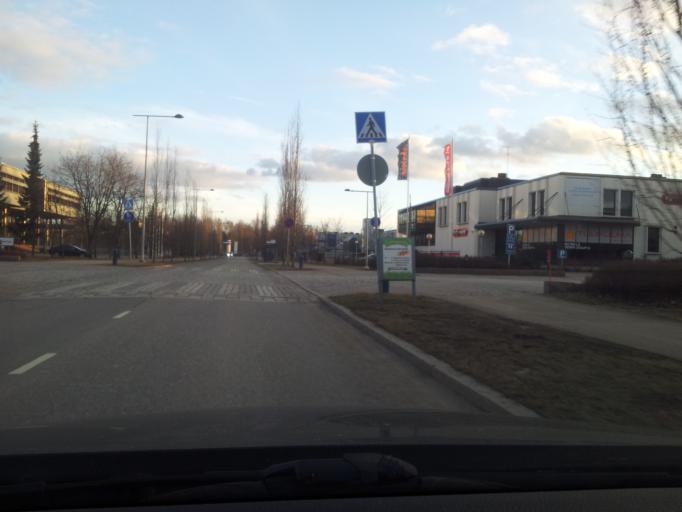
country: FI
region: Uusimaa
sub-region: Helsinki
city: Koukkuniemi
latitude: 60.1770
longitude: 24.7587
